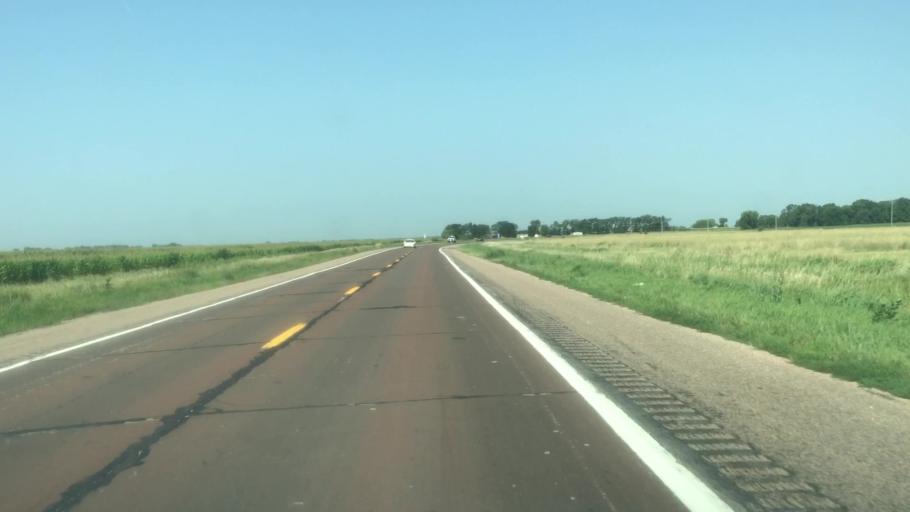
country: US
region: Nebraska
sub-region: Hall County
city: Grand Island
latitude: 40.9677
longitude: -98.4936
